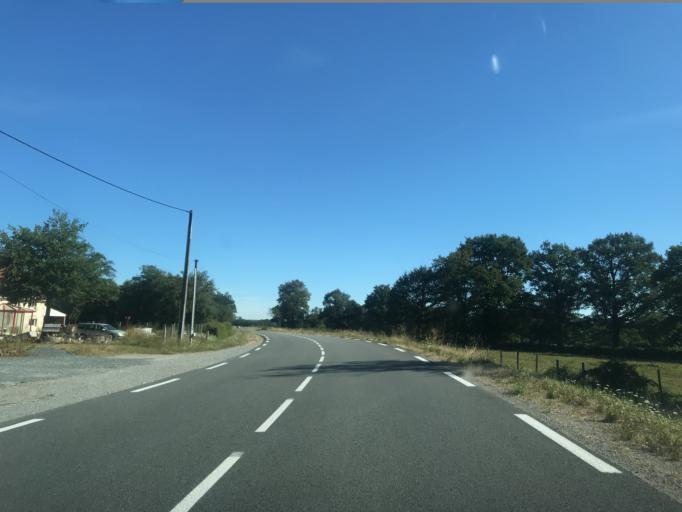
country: FR
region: Limousin
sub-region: Departement de la Creuse
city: Gouzon
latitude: 46.1709
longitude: 2.2218
